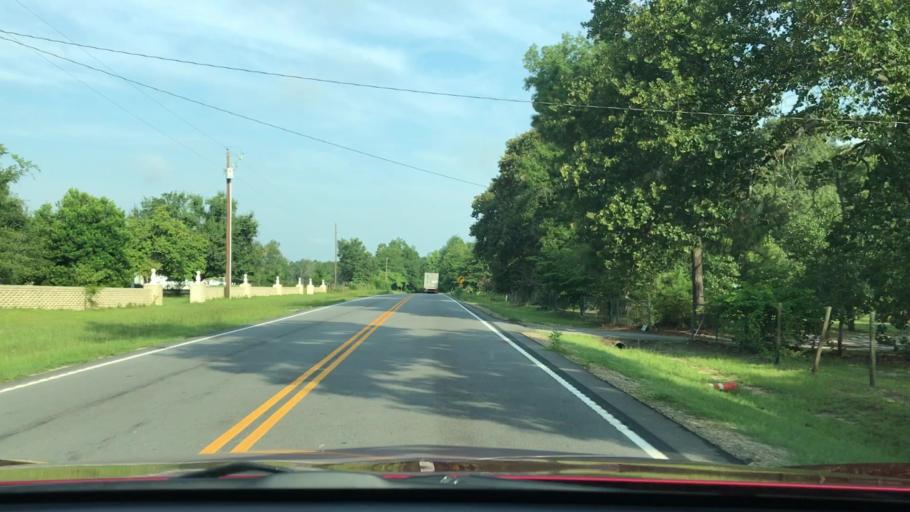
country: US
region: South Carolina
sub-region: Bamberg County
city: Denmark
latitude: 33.5431
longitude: -81.1453
